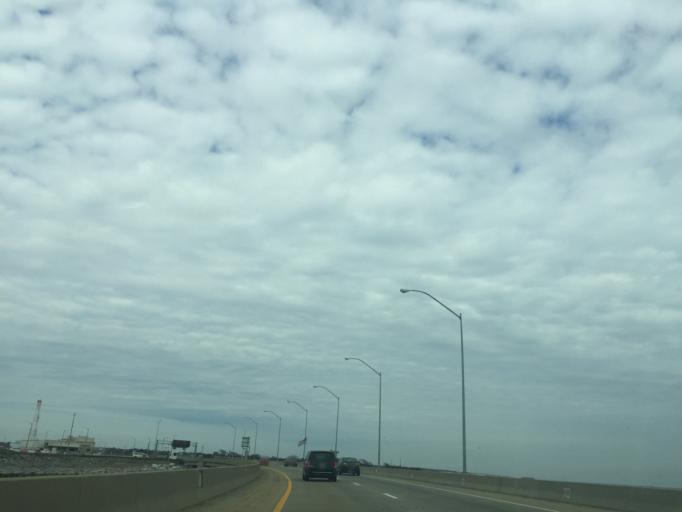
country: US
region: Virginia
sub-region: City of Hampton
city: East Hampton
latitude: 36.9810
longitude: -76.3005
